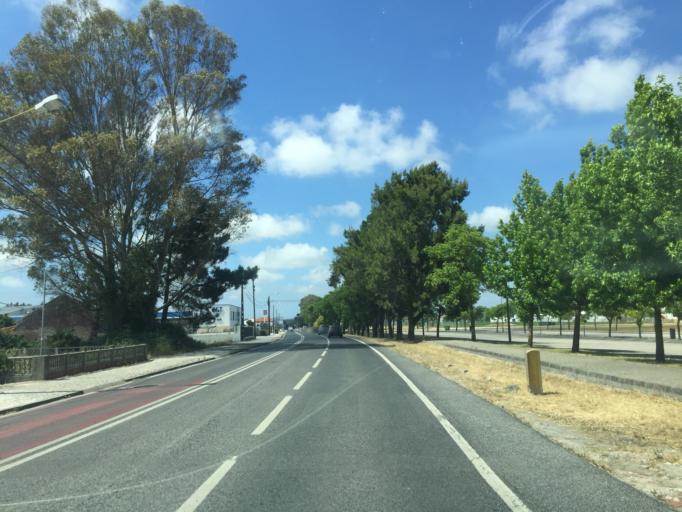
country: PT
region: Leiria
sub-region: Marinha Grande
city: Marinha Grande
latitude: 39.7364
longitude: -8.9329
